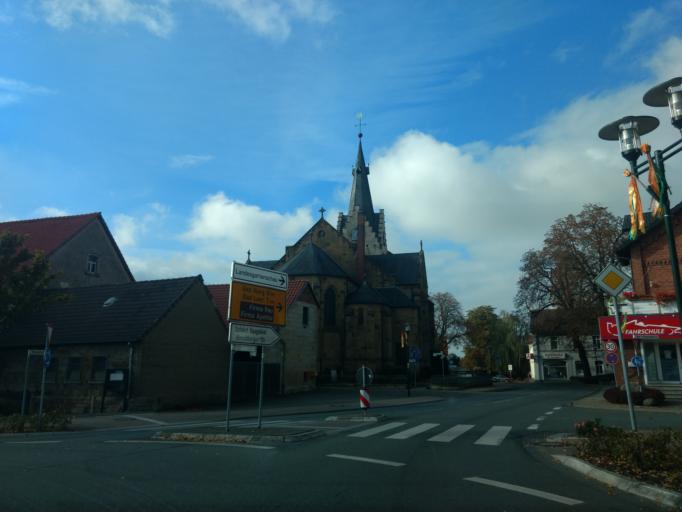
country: DE
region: Lower Saxony
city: Hilter
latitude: 52.1395
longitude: 8.1456
